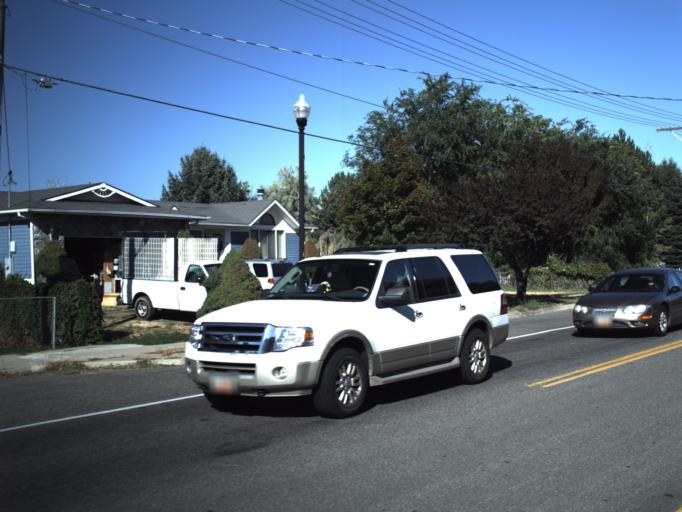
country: US
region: Utah
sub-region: Davis County
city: Clinton
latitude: 41.1398
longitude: -112.0526
